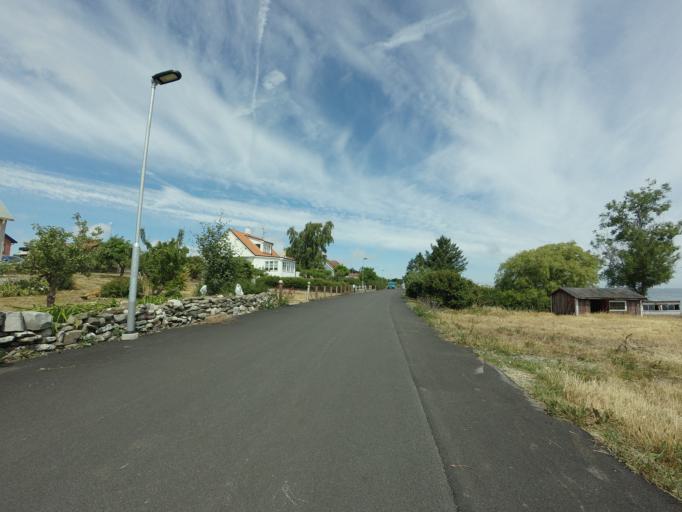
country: SE
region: Skane
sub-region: Simrishamns Kommun
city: Simrishamn
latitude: 55.5451
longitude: 14.3569
